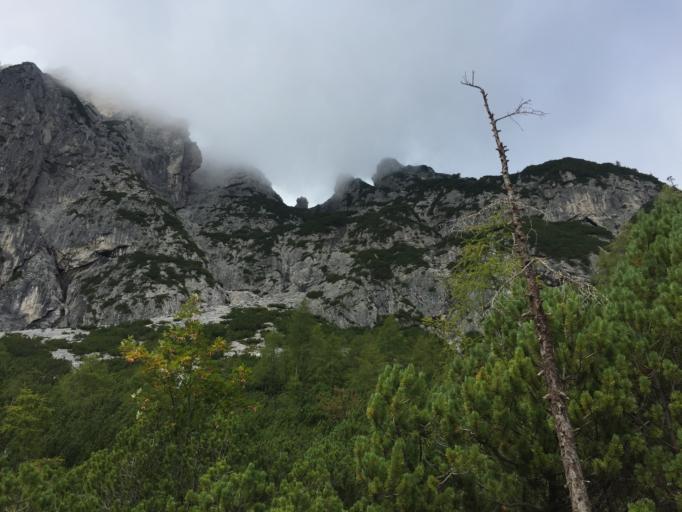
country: IT
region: Friuli Venezia Giulia
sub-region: Provincia di Udine
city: Tarvisio
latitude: 46.4599
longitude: 13.5941
